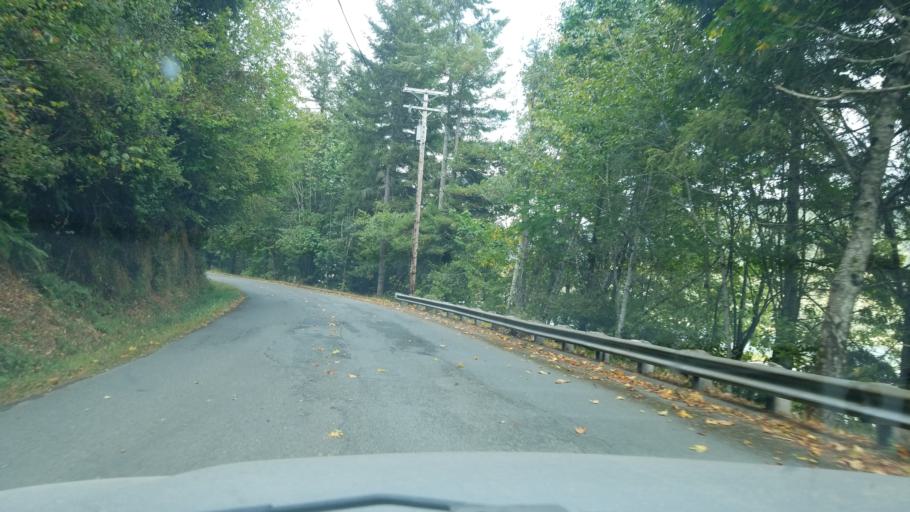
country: US
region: California
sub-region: Del Norte County
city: Bertsch-Oceanview
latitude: 41.5148
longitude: -124.0381
